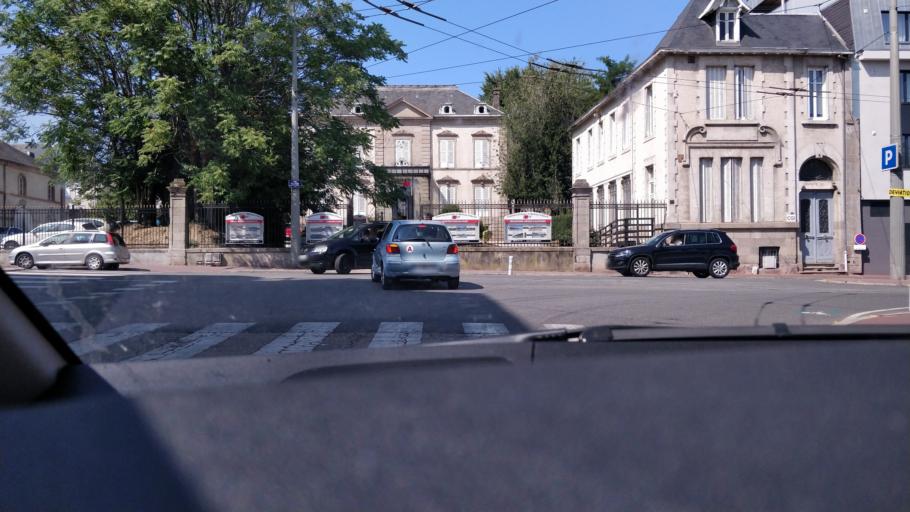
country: FR
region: Limousin
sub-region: Departement de la Haute-Vienne
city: Limoges
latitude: 45.8353
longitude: 1.2620
